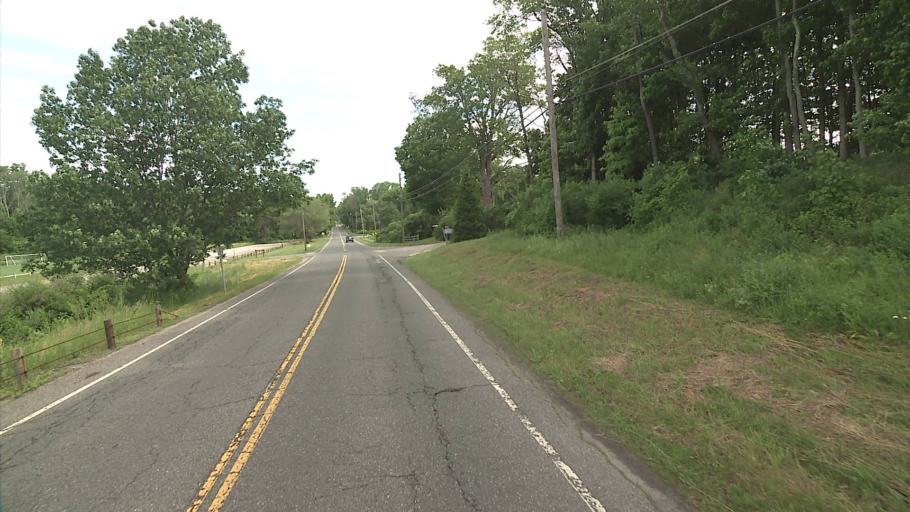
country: US
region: Connecticut
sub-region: Litchfield County
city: Litchfield
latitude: 41.7284
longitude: -73.1855
